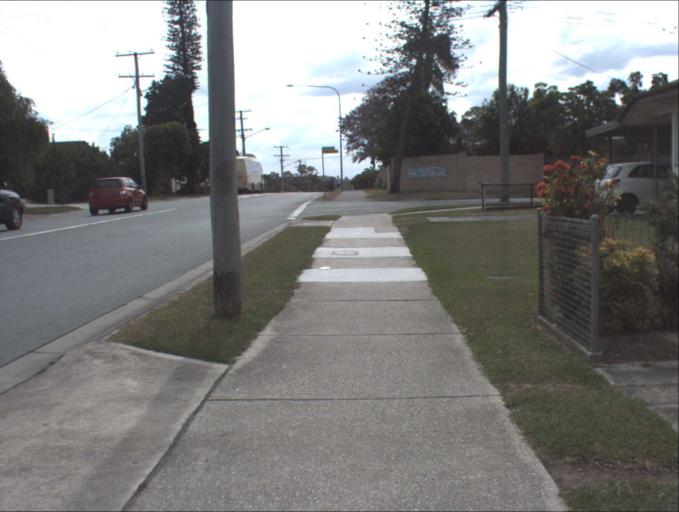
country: AU
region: Queensland
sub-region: Logan
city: Beenleigh
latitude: -27.7084
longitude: 153.2016
